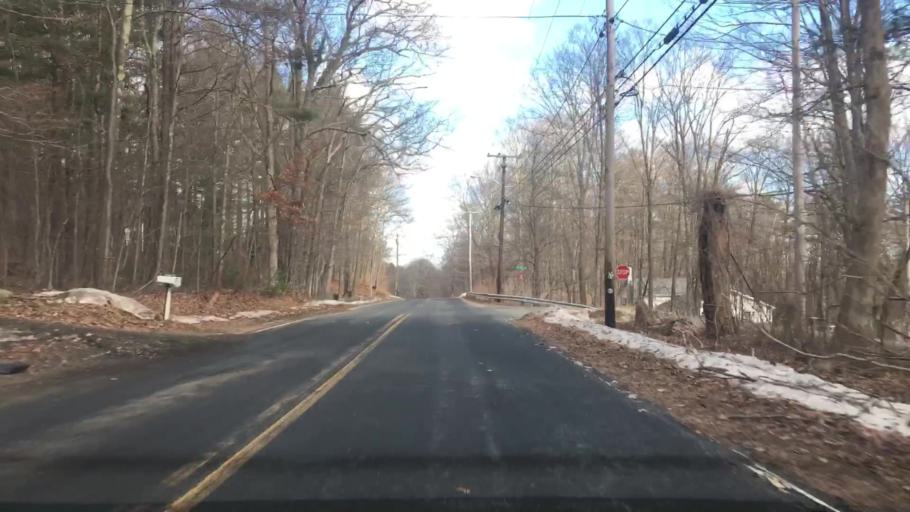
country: US
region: Massachusetts
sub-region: Hampden County
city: Wales
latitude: 42.0508
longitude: -72.2289
